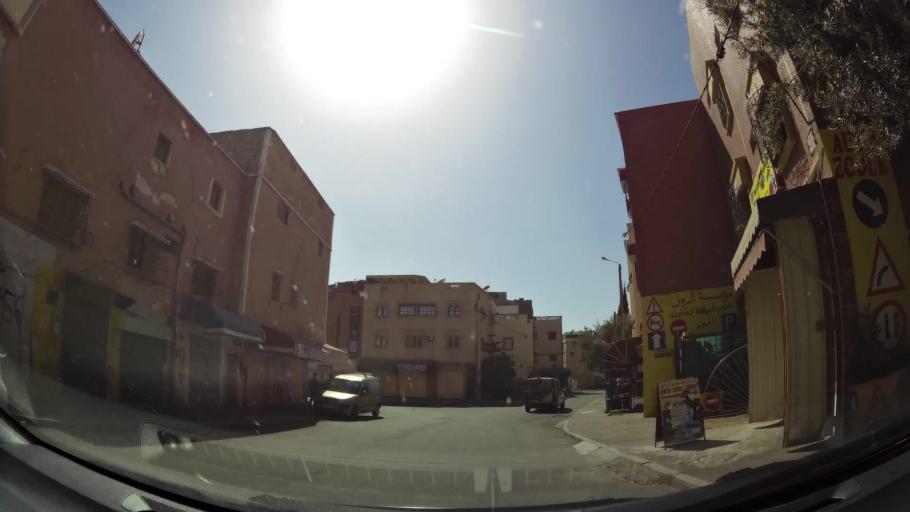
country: MA
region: Souss-Massa-Draa
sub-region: Inezgane-Ait Mellou
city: Inezgane
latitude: 30.3562
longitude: -9.5491
